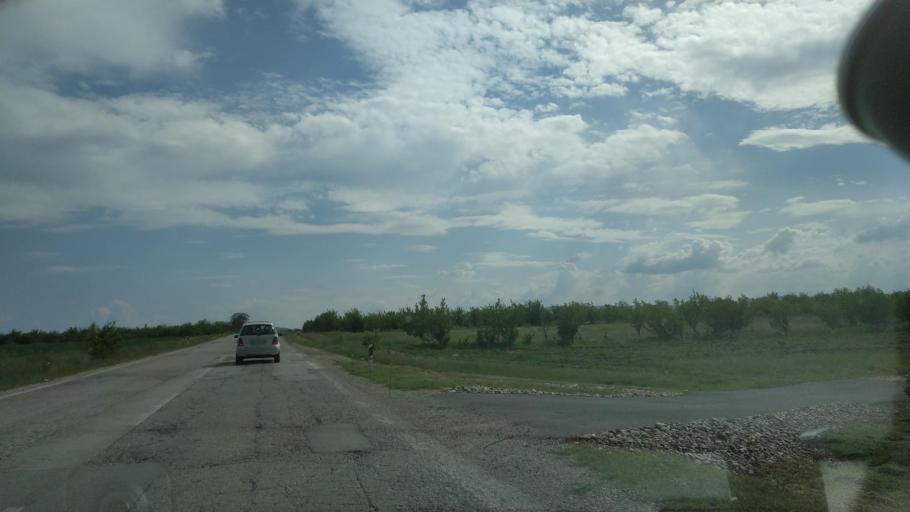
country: RS
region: Central Serbia
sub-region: Nisavski Okrug
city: Merosina
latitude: 43.2740
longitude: 21.6844
